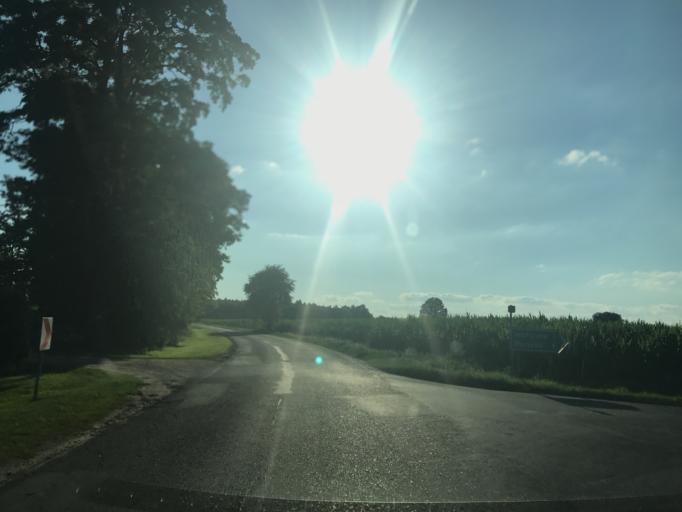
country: PL
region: Greater Poland Voivodeship
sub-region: Powiat turecki
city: Wladyslawow
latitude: 52.1005
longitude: 18.3997
